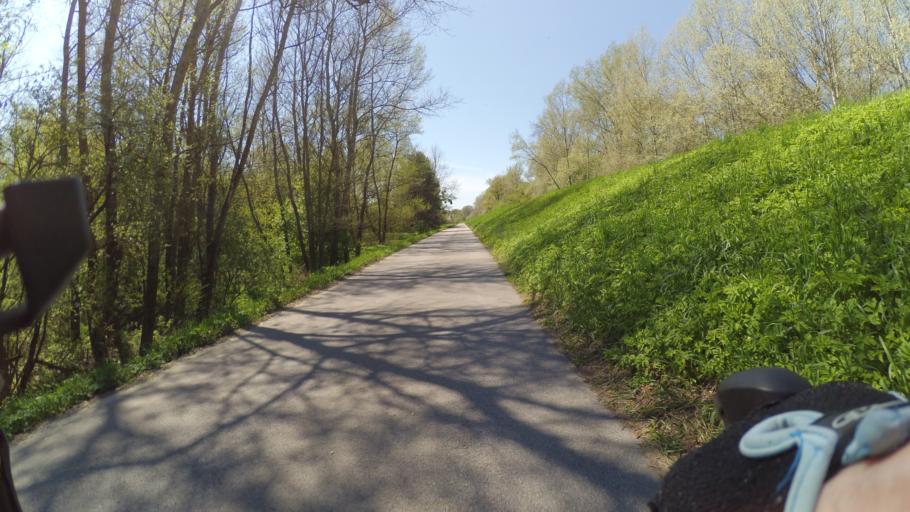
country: PL
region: Masovian Voivodeship
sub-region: Powiat plonski
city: Zaluski
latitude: 52.4062
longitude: 20.4752
